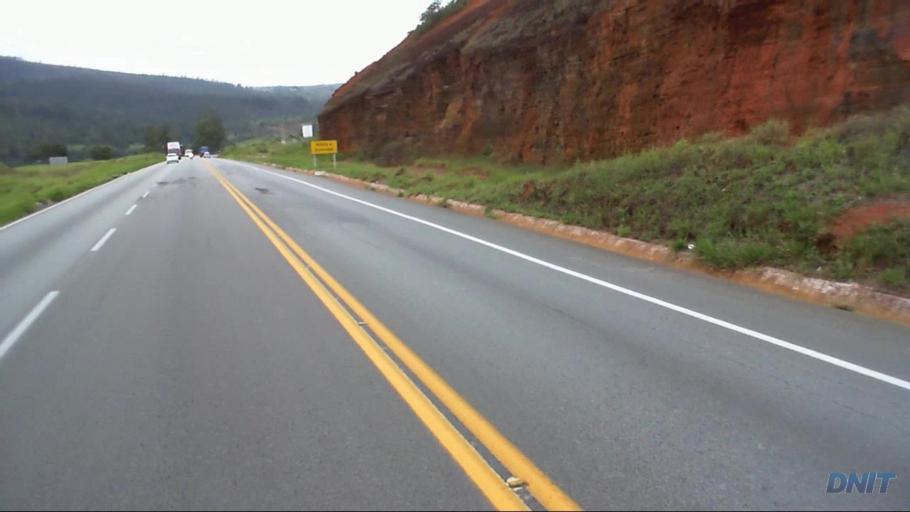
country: BR
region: Minas Gerais
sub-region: Joao Monlevade
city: Joao Monlevade
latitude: -19.8312
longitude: -43.0950
